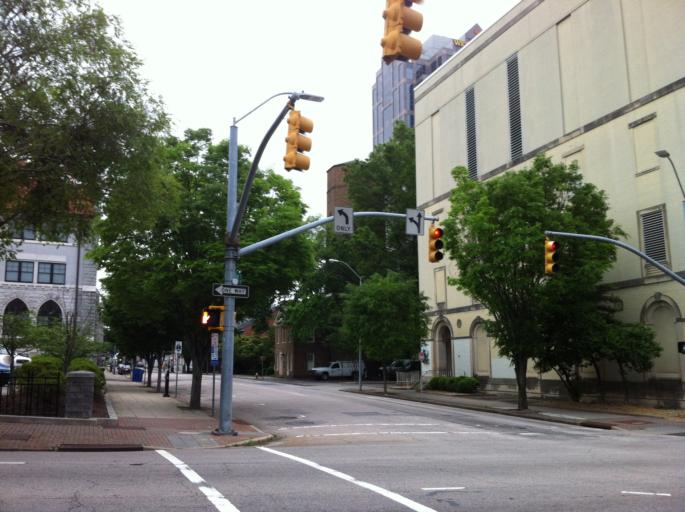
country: US
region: North Carolina
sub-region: Wake County
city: Raleigh
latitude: 35.7798
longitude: -78.6418
